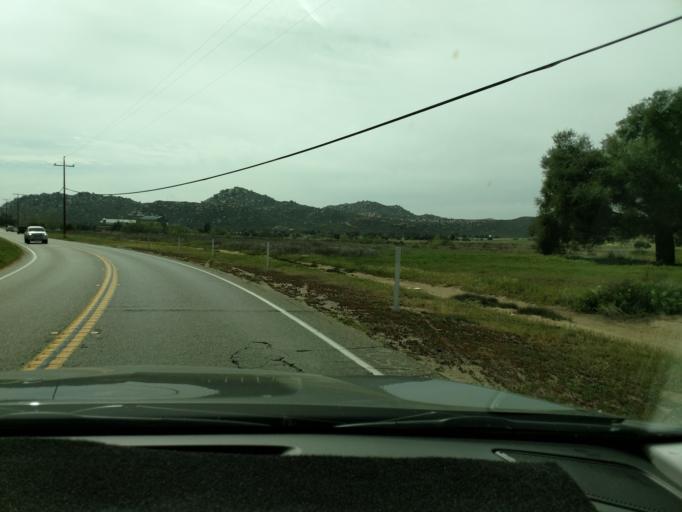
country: US
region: California
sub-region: San Diego County
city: Ramona
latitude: 32.9427
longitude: -116.8612
